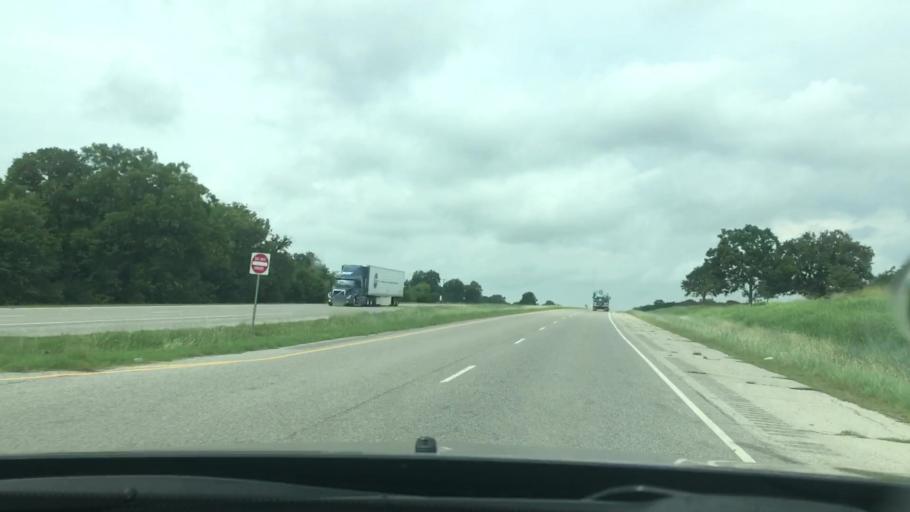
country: US
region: Oklahoma
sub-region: Carter County
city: Wilson
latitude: 34.1731
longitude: -97.4221
